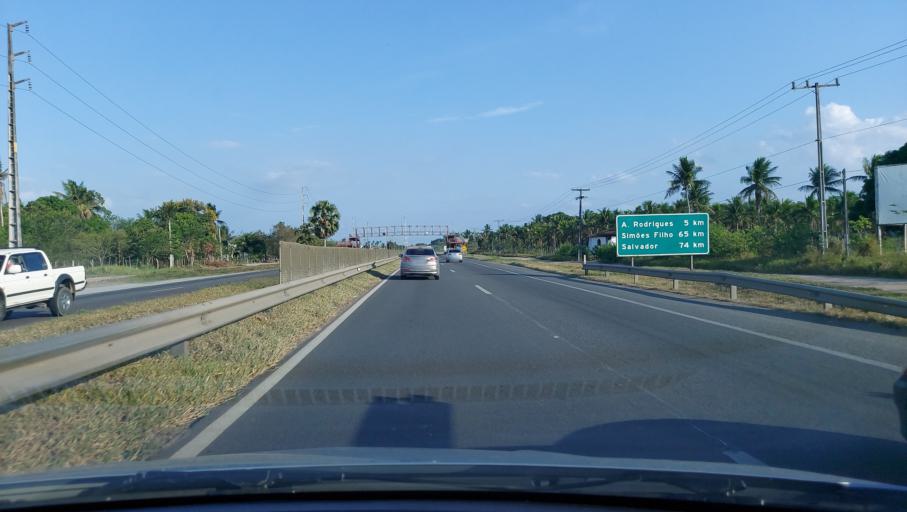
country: BR
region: Bahia
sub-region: Conceicao Do Jacuipe
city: Conceicao do Jacuipe
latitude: -12.3820
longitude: -38.7968
